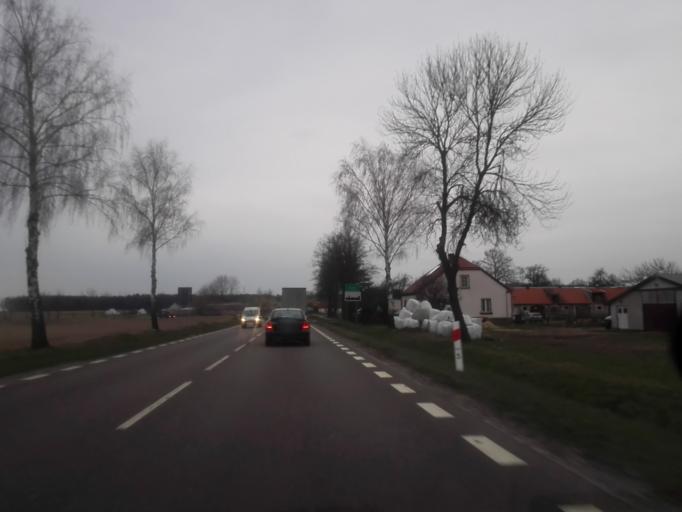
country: PL
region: Podlasie
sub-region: Powiat grajewski
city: Szczuczyn
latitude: 53.5963
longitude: 22.3508
